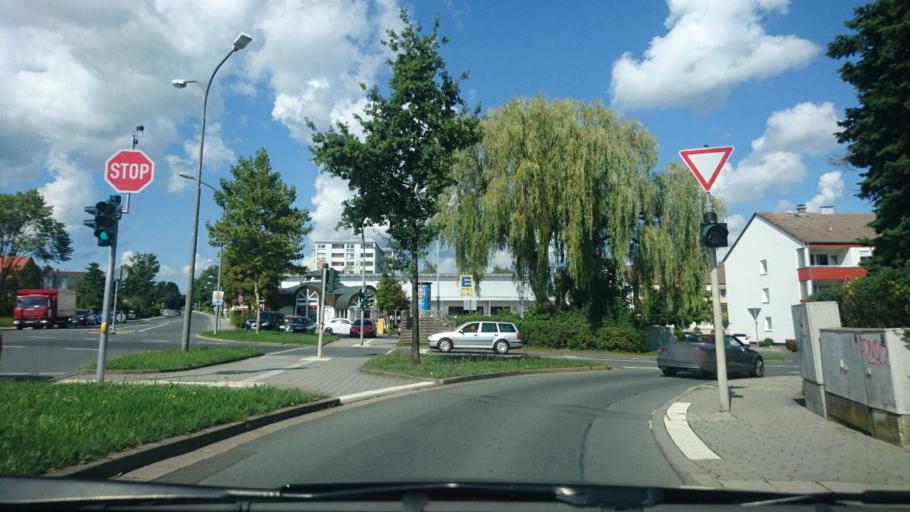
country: DE
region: Bavaria
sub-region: Upper Franconia
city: Heinersreuth
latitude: 49.9460
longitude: 11.5464
